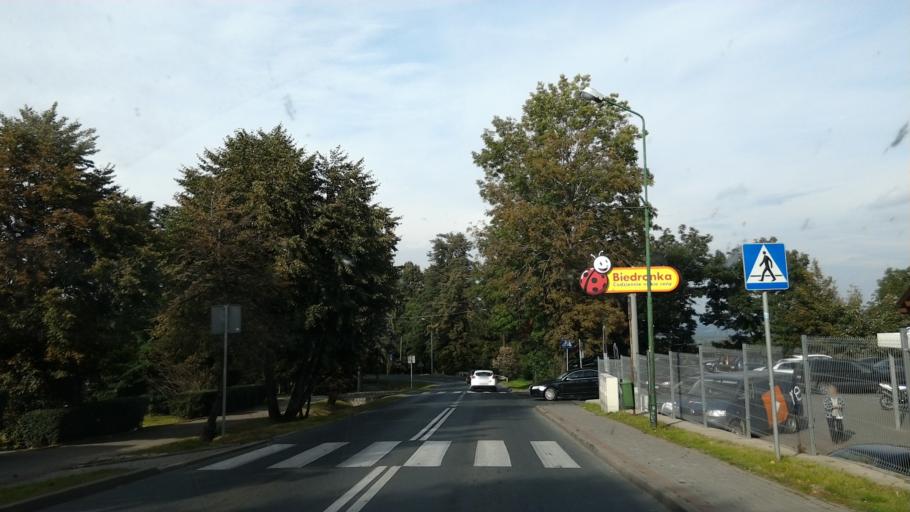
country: PL
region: Lower Silesian Voivodeship
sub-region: Powiat jeleniogorski
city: Karpacz
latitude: 50.7814
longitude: 15.7631
